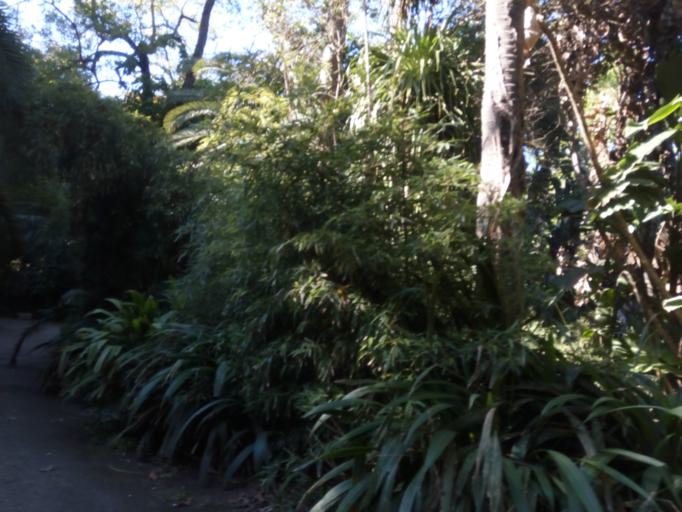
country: DZ
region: Alger
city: Algiers
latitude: 36.7460
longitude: 3.0768
